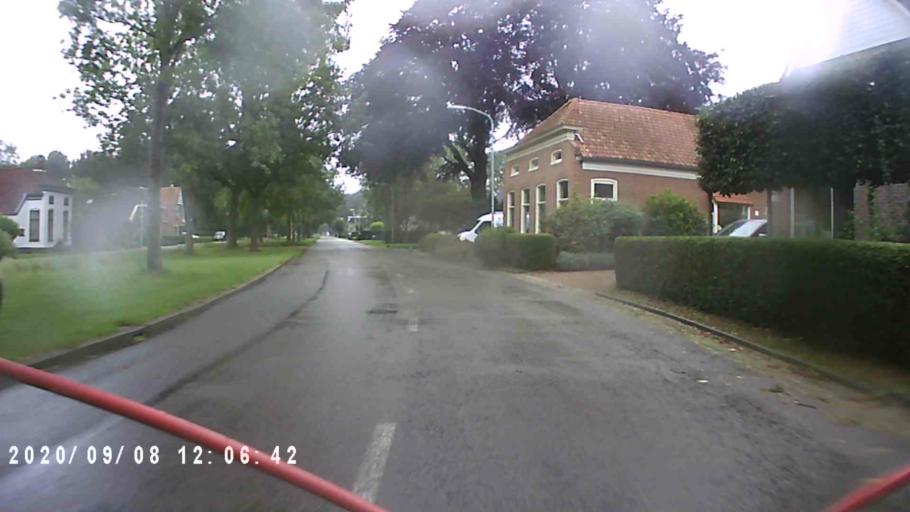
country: NL
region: Groningen
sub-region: Gemeente Veendam
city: Veendam
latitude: 53.1078
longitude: 6.8259
